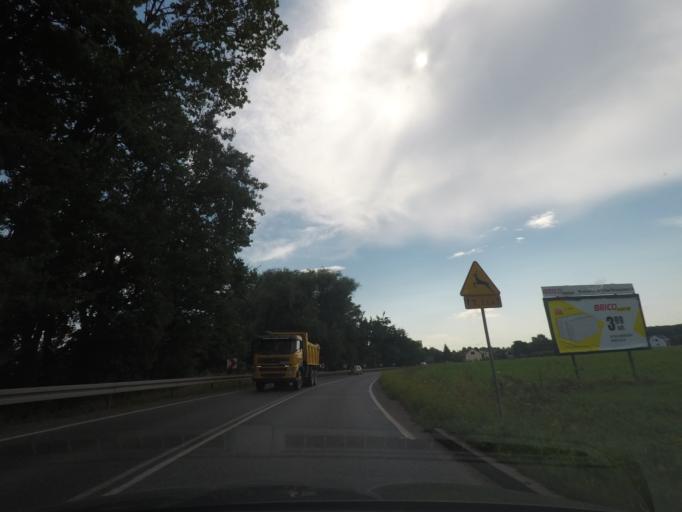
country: PL
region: Lesser Poland Voivodeship
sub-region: Powiat oswiecimski
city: Przecieszyn
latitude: 49.9963
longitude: 19.1727
